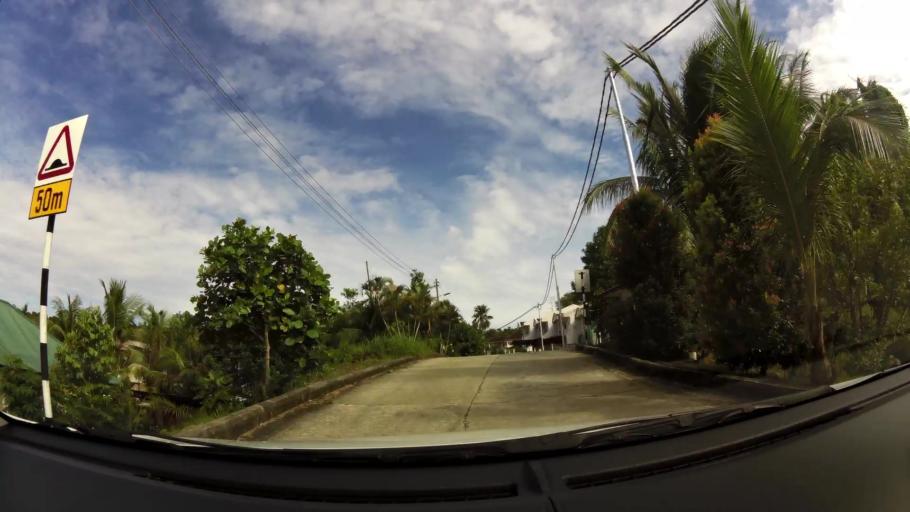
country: BN
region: Brunei and Muara
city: Bandar Seri Begawan
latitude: 4.8981
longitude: 114.9700
